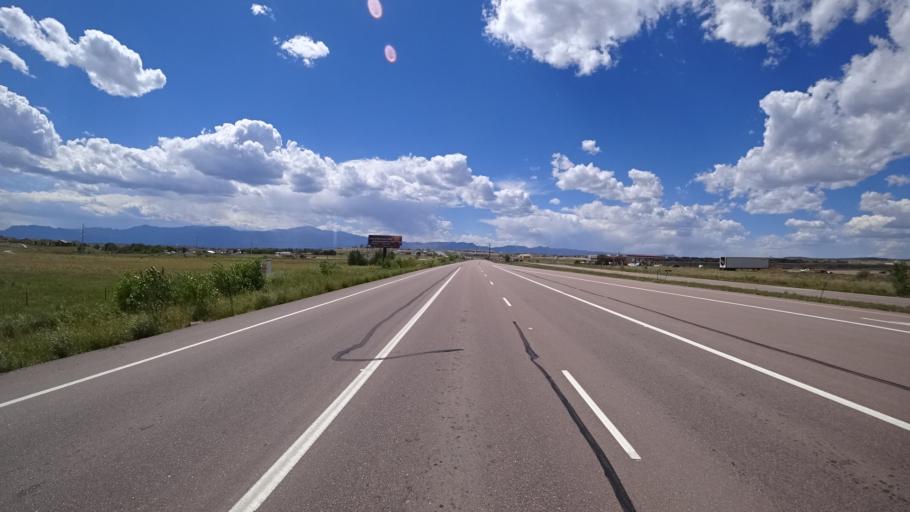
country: US
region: Colorado
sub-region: El Paso County
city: Black Forest
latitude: 38.9407
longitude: -104.6791
